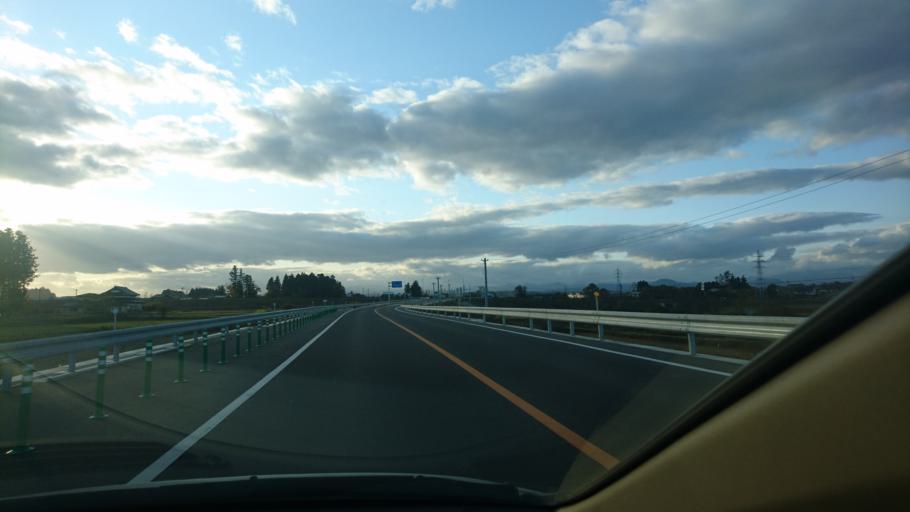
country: JP
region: Miyagi
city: Furukawa
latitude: 38.7385
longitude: 141.0418
